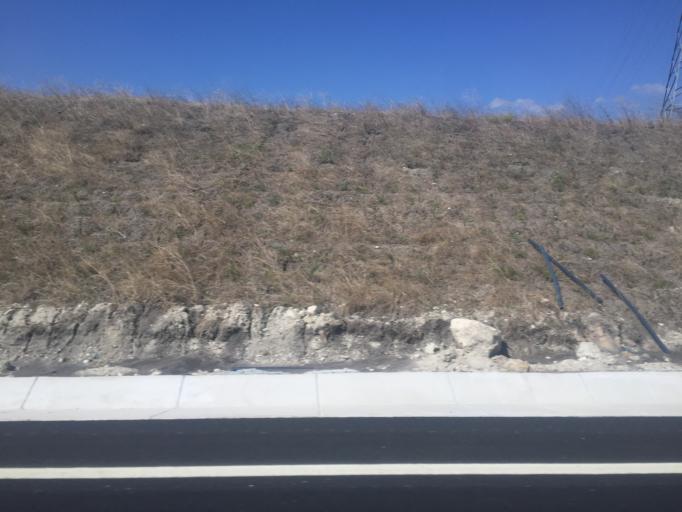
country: TR
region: Balikesir
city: Susurluk
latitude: 39.9643
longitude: 28.1642
